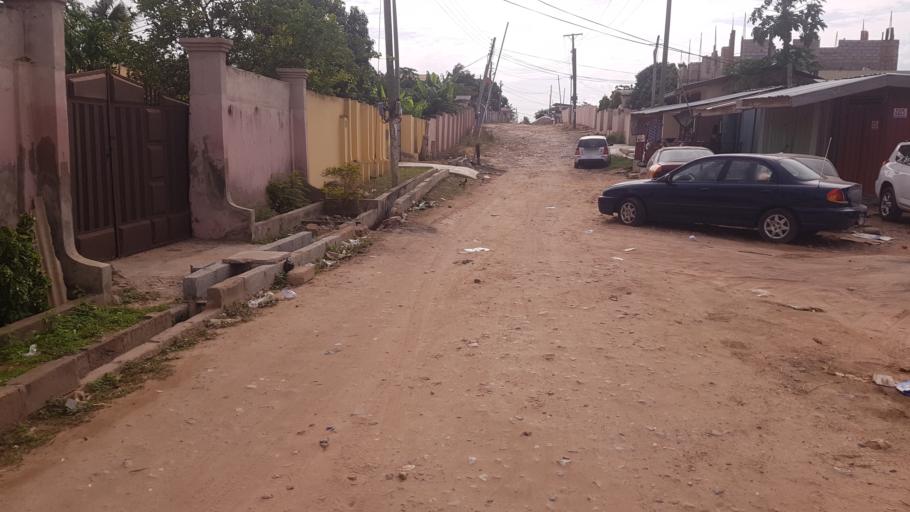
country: GH
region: Greater Accra
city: Gbawe
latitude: 5.5503
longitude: -0.3402
